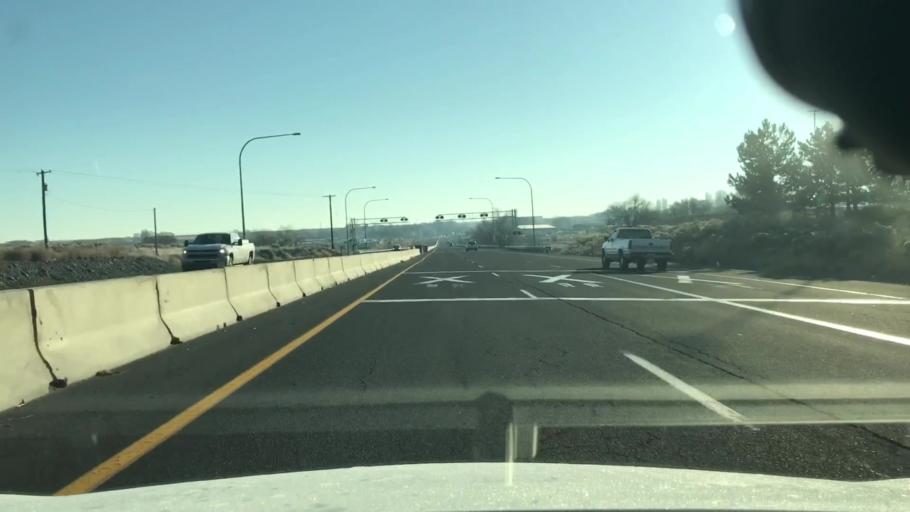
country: US
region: Washington
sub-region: Grant County
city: Moses Lake
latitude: 47.1428
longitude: -119.2734
